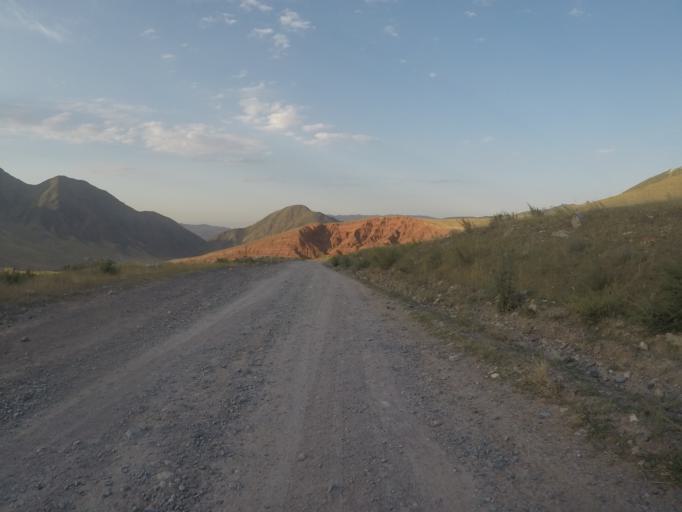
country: KG
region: Chuy
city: Bishkek
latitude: 42.6592
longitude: 74.6511
